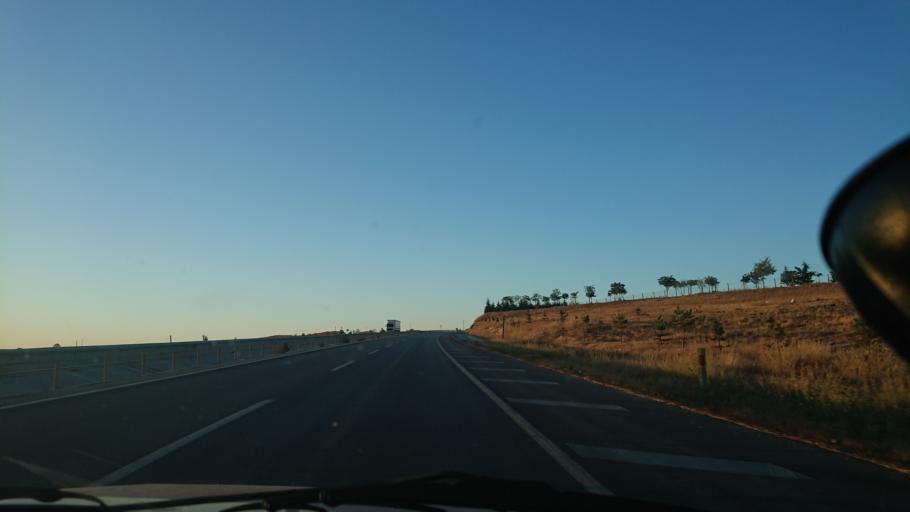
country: TR
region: Eskisehir
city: Mahmudiye
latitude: 39.5013
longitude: 30.9663
